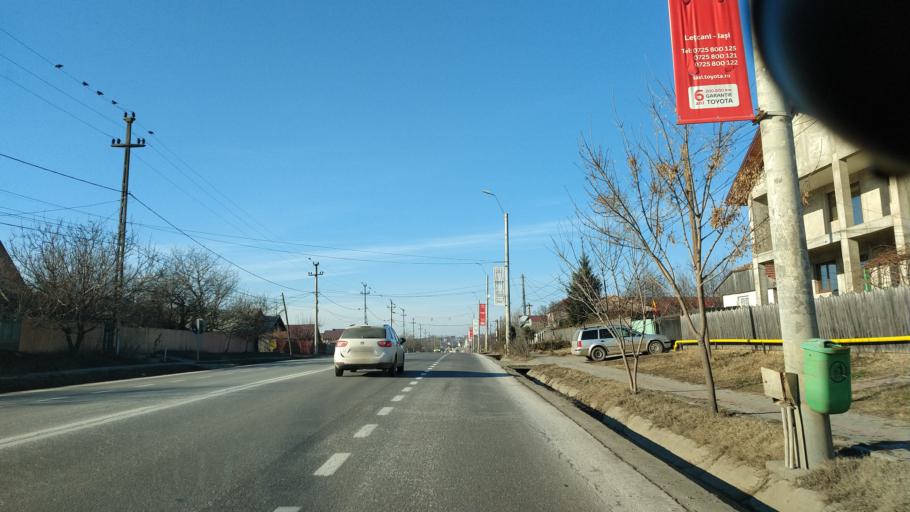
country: RO
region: Iasi
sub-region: Comuna Letcani
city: Letcani
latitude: 47.1924
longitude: 27.4240
